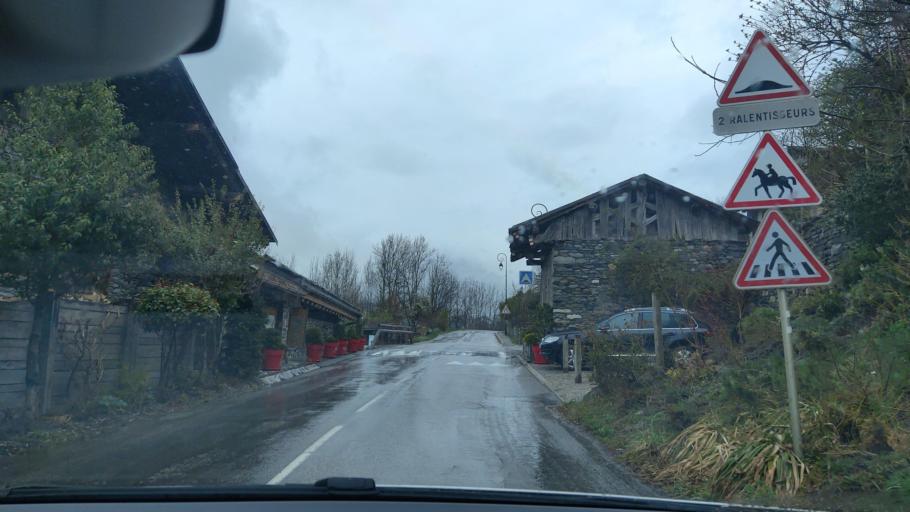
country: FR
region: Rhone-Alpes
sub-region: Departement de la Savoie
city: Bourg-Saint-Maurice
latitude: 45.5937
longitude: 6.7575
